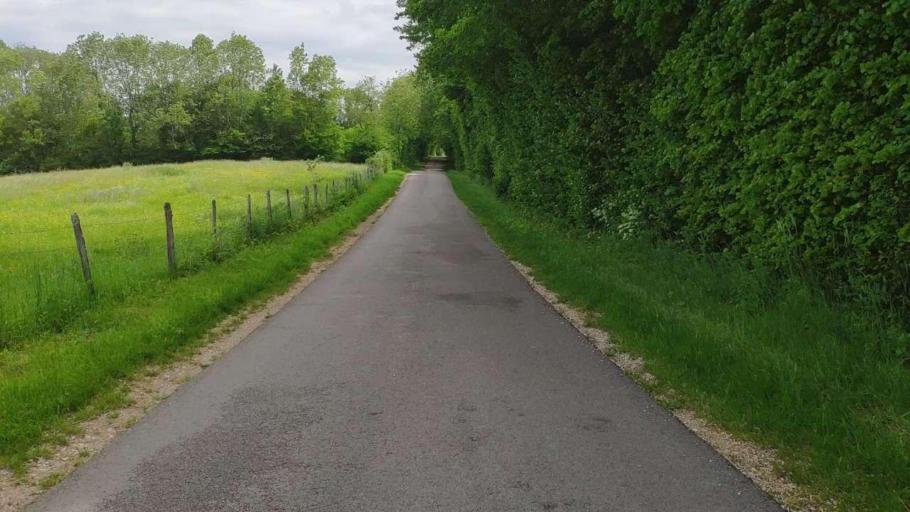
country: FR
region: Franche-Comte
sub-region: Departement du Jura
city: Poligny
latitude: 46.7842
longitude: 5.6670
